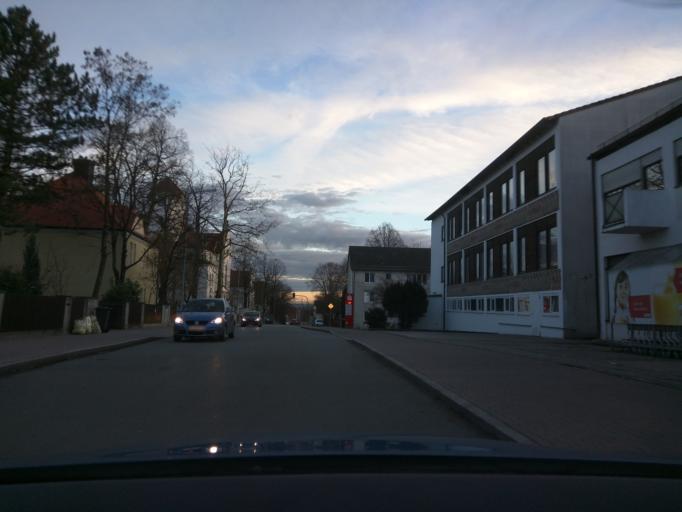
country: DE
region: Bavaria
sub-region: Upper Bavaria
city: Freising
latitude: 48.4074
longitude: 11.7377
